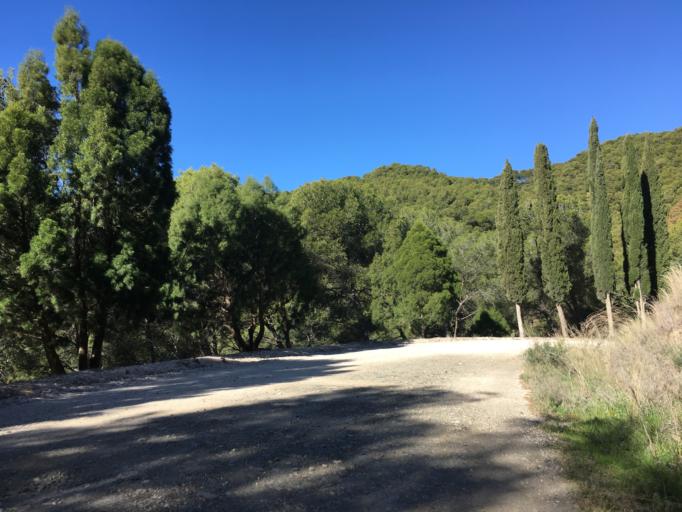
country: ES
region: Andalusia
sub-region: Provincia de Malaga
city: Malaga
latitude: 36.7813
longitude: -4.3861
